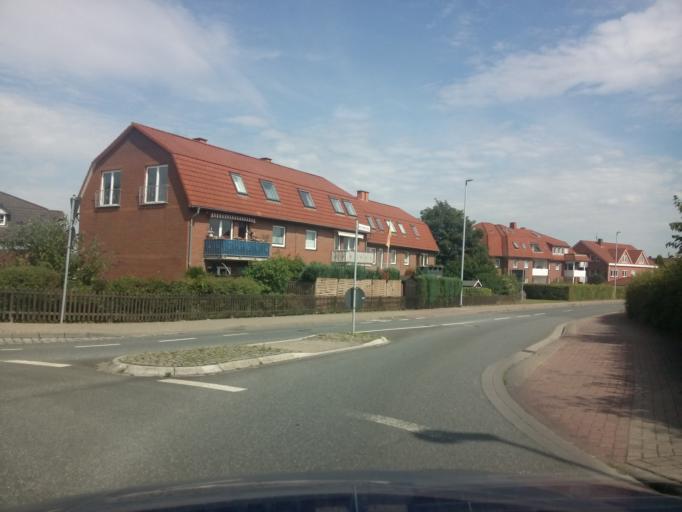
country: DE
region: Lower Saxony
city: Osterholz-Scharmbeck
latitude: 53.2372
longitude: 8.7953
